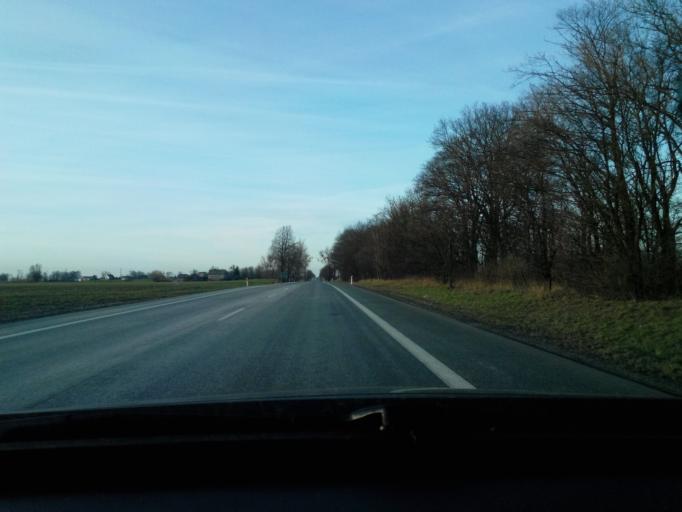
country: PL
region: Kujawsko-Pomorskie
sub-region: Powiat wloclawski
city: Lubien Kujawski
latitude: 52.4538
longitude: 19.1587
